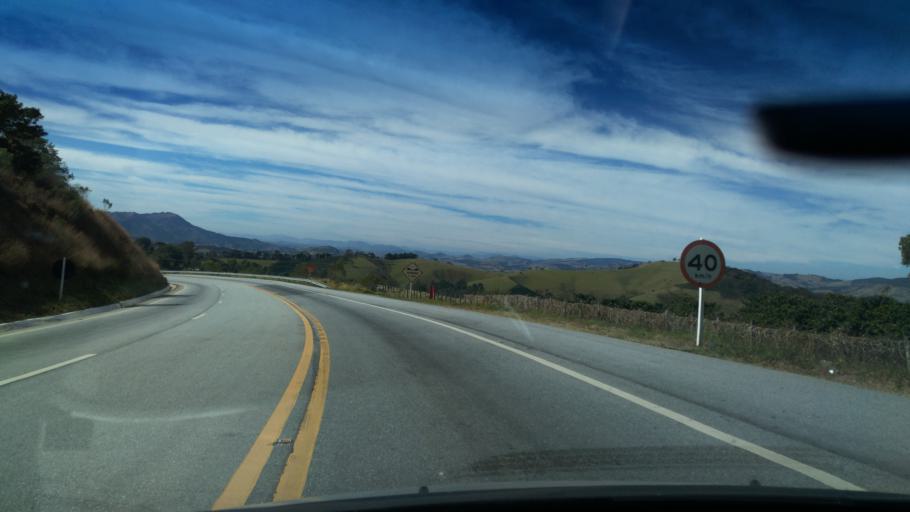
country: BR
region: Minas Gerais
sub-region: Borda Da Mata
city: Borda da Mata
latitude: -22.1350
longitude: -46.1693
